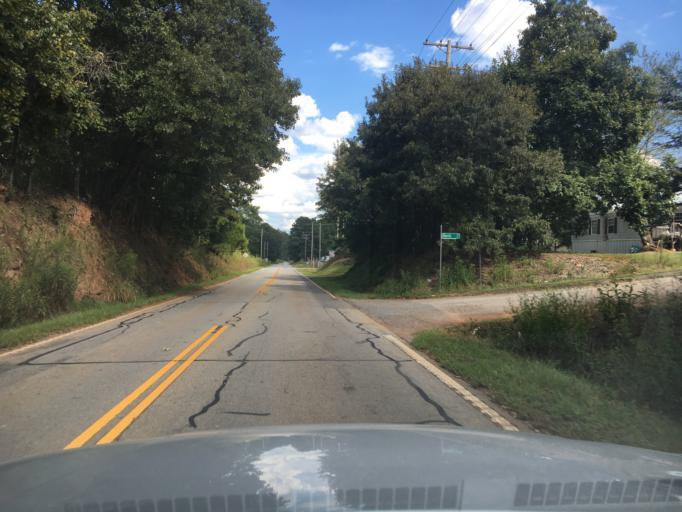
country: US
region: South Carolina
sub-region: Oconee County
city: Utica
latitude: 34.7119
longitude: -82.8996
